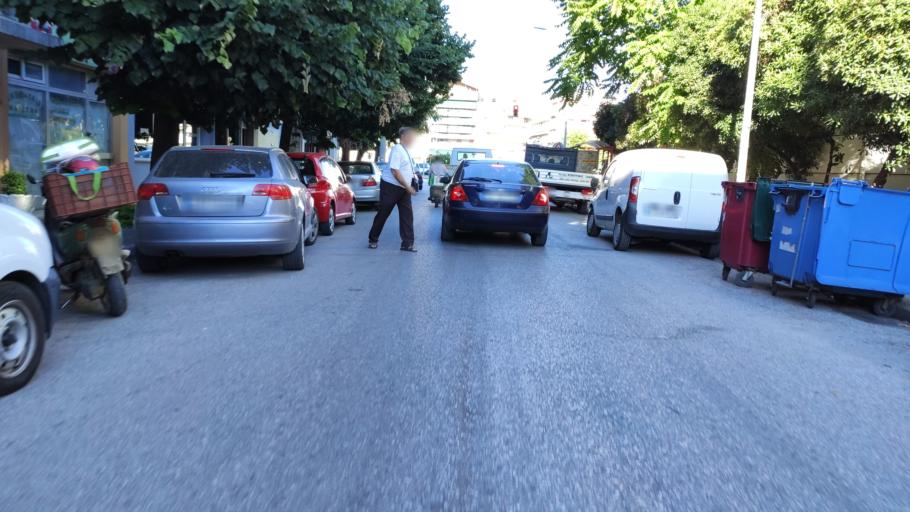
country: GR
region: East Macedonia and Thrace
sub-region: Nomos Rodopis
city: Komotini
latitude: 41.1176
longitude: 25.3963
